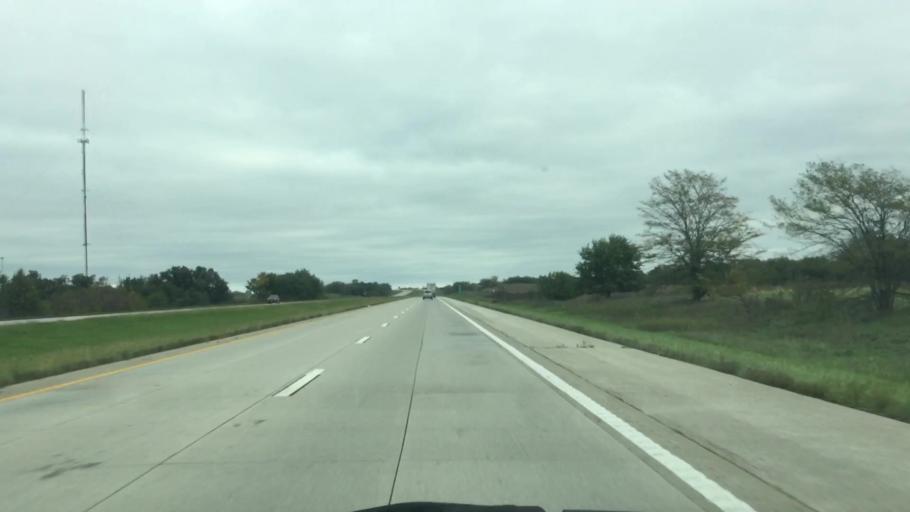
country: US
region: Missouri
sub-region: Daviess County
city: Gallatin
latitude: 39.9629
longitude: -94.1010
